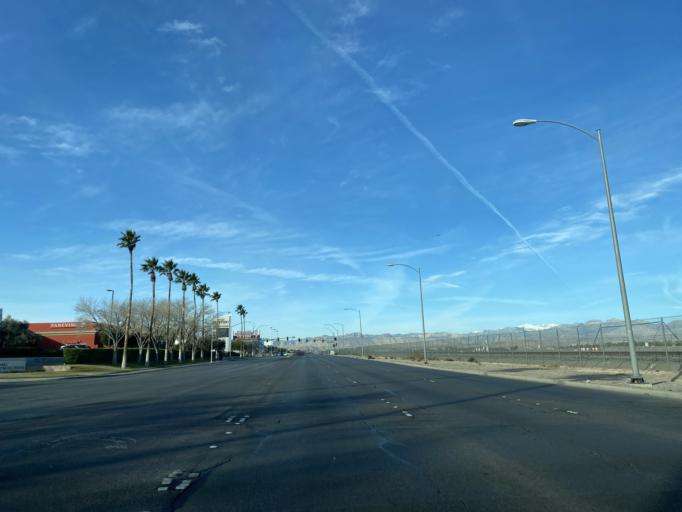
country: US
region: Nevada
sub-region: Clark County
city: Paradise
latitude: 36.0713
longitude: -115.1611
